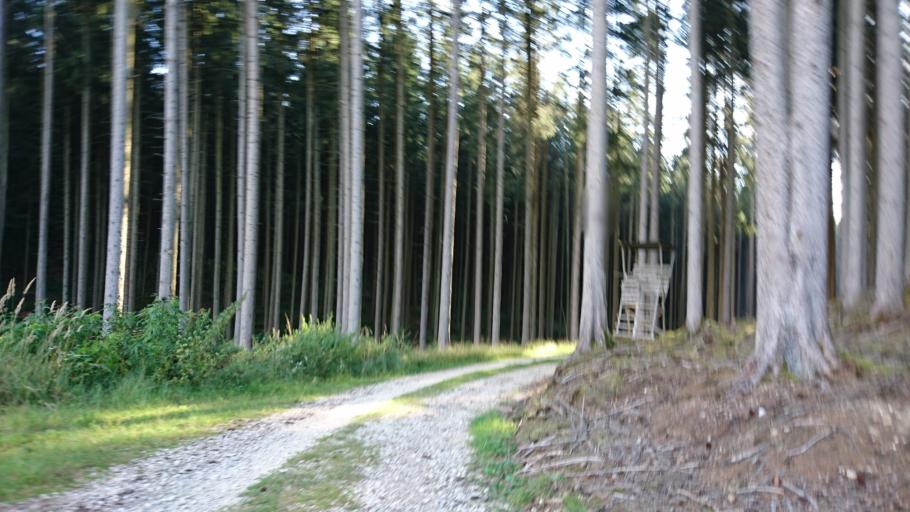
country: DE
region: Bavaria
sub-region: Swabia
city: Welden
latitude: 48.4327
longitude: 10.6281
